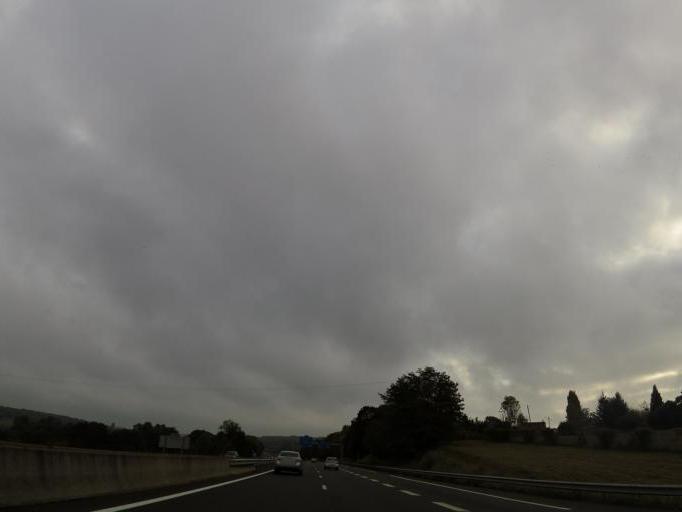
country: FR
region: Ile-de-France
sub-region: Departement de Seine-et-Marne
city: Villiers-sur-Morin
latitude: 48.8780
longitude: 2.8810
